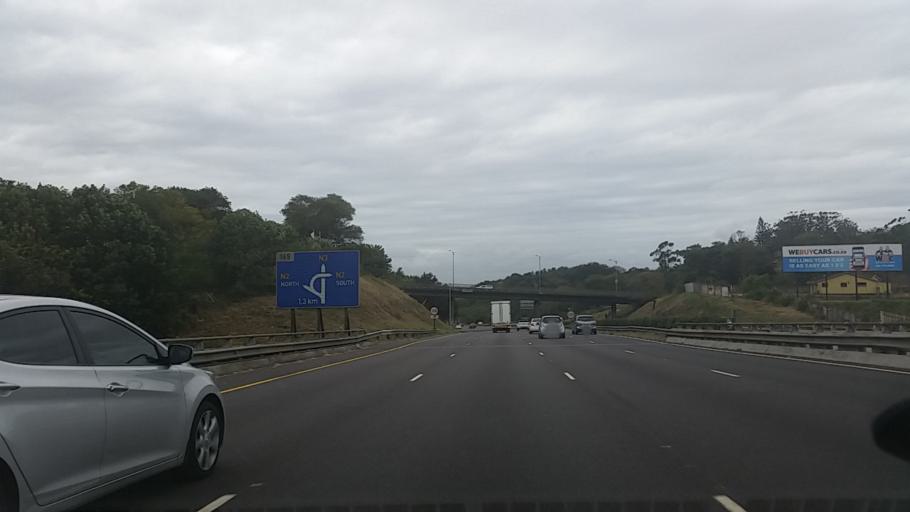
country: ZA
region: KwaZulu-Natal
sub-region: eThekwini Metropolitan Municipality
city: Berea
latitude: -29.8453
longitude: 30.9392
